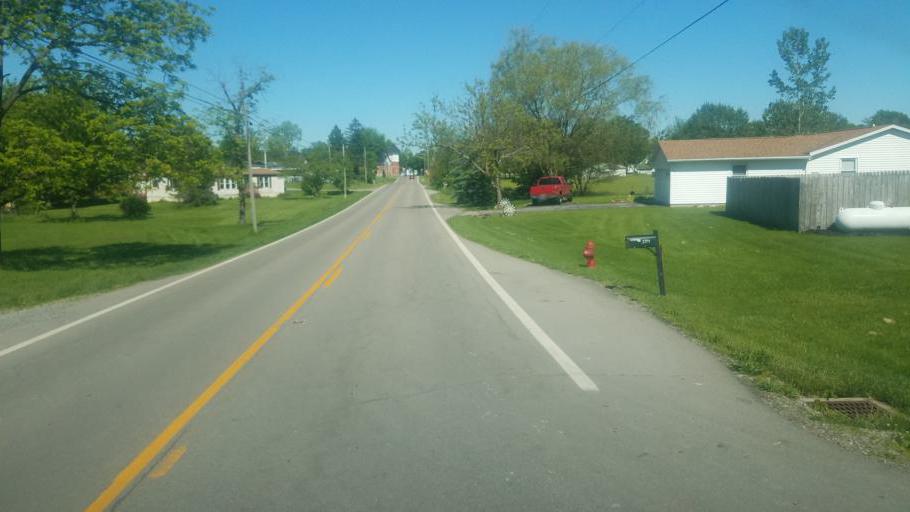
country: US
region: Ohio
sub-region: Logan County
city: Northwood
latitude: 40.4599
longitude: -83.6761
